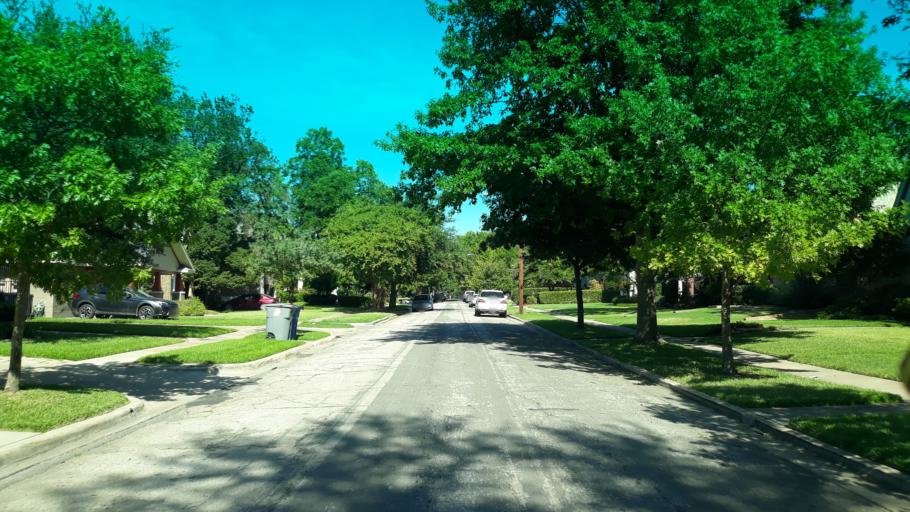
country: US
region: Texas
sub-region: Dallas County
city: Highland Park
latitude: 32.8201
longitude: -96.7580
